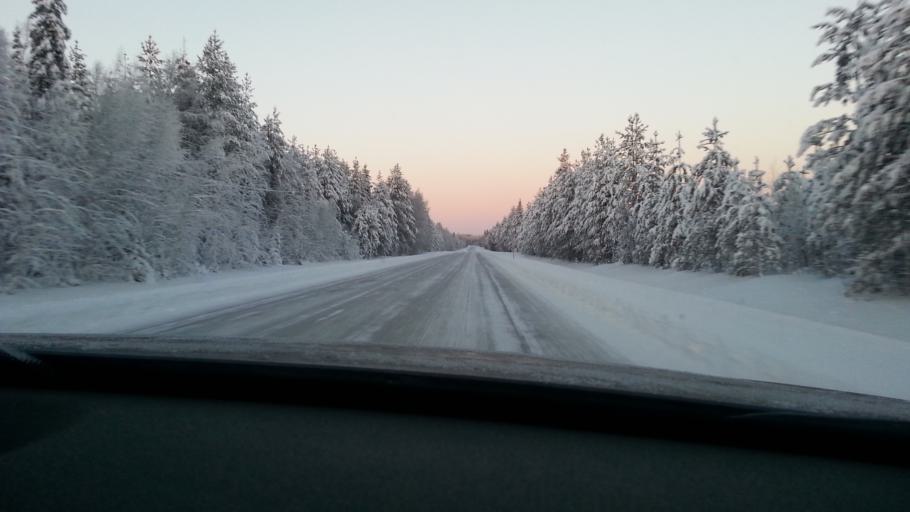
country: FI
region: Lapland
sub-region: Tunturi-Lappi
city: Kittilae
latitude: 67.2217
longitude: 24.9236
